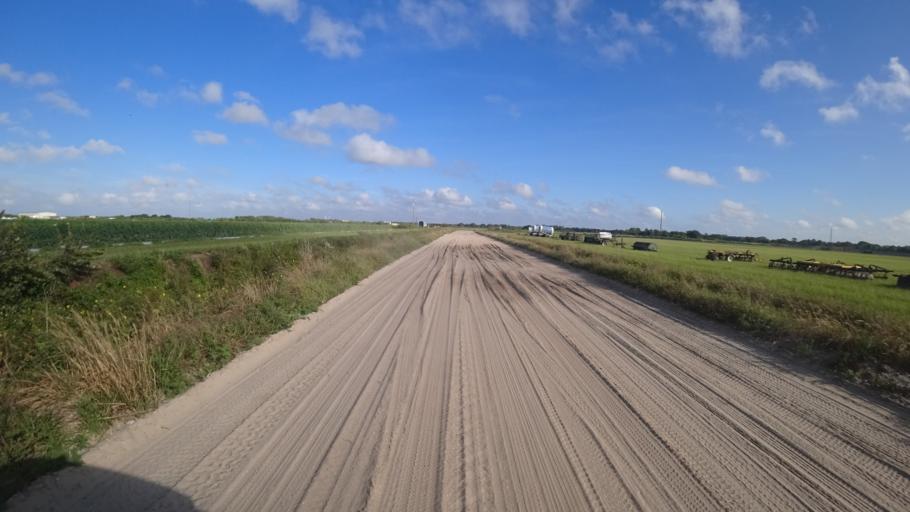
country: US
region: Florida
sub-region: Hillsborough County
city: Wimauma
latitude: 27.5407
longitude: -82.3179
